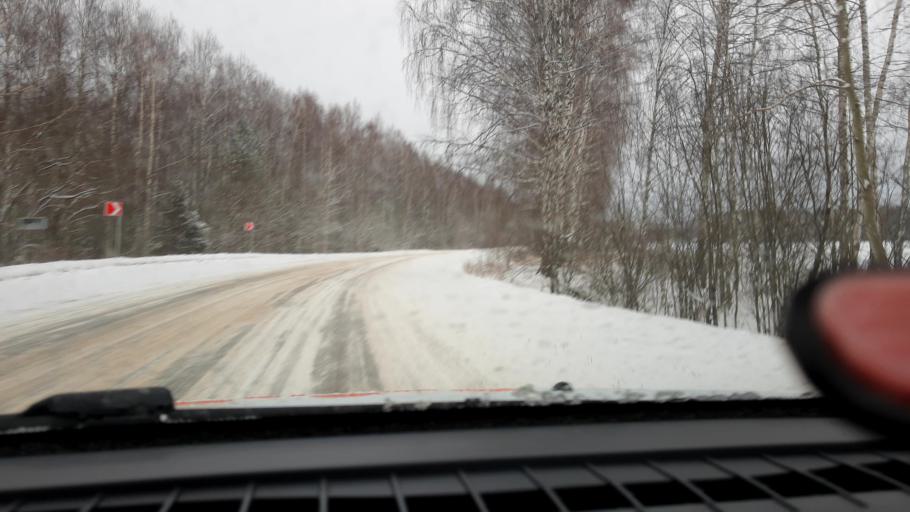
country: RU
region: Nizjnij Novgorod
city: Pamyat' Parizhskoy Kommuny
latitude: 56.2507
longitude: 44.4778
